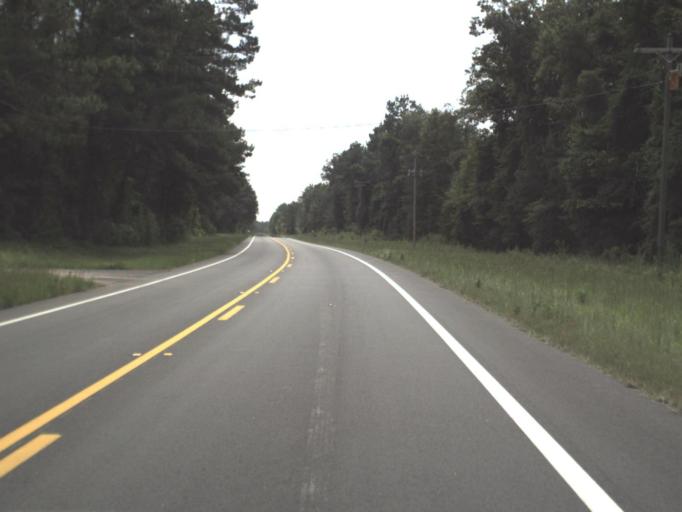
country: US
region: Florida
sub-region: Jefferson County
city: Monticello
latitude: 30.4851
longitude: -83.7000
